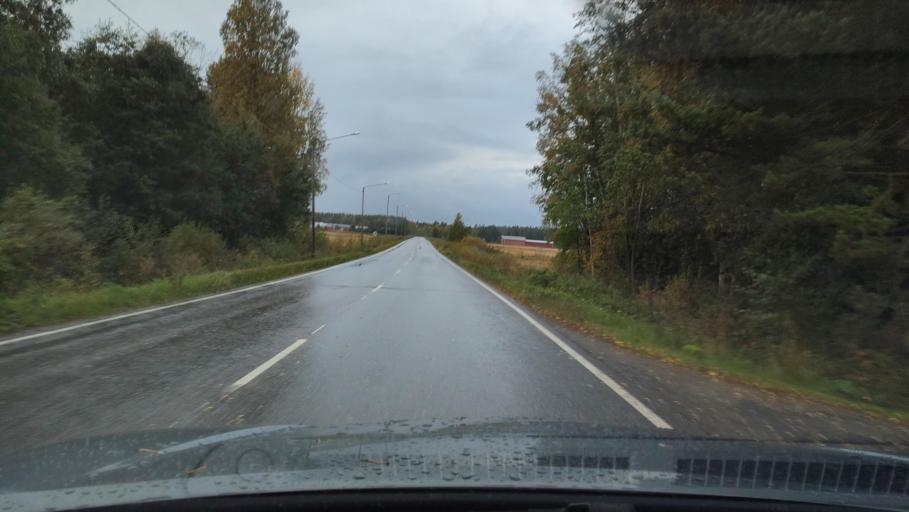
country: FI
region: Southern Ostrobothnia
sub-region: Suupohja
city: Karijoki
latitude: 62.2357
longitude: 21.6149
